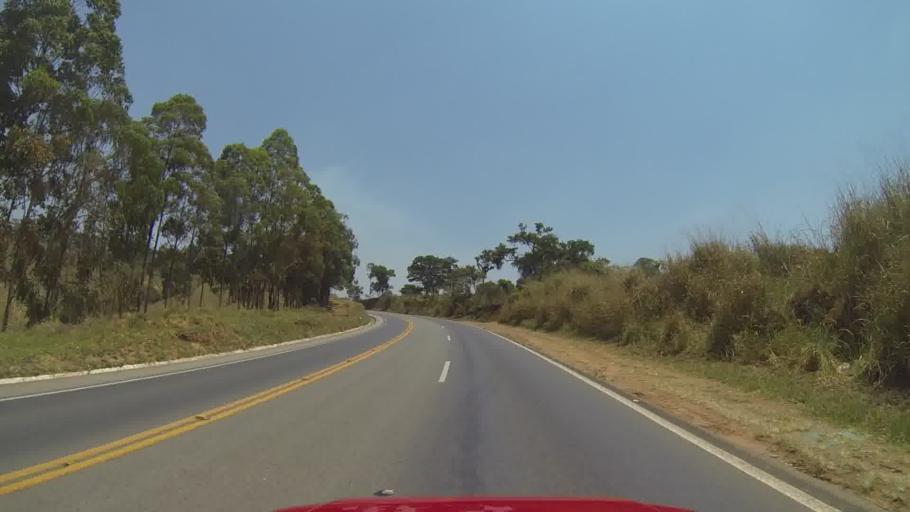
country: BR
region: Minas Gerais
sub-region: Itapecerica
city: Itapecerica
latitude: -20.3396
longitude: -45.2407
